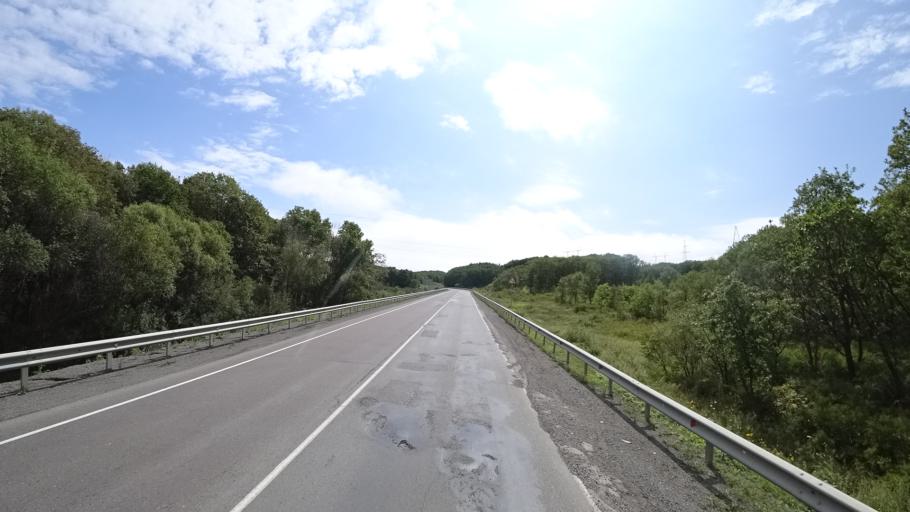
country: RU
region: Primorskiy
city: Lyalichi
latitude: 44.1355
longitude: 132.4278
